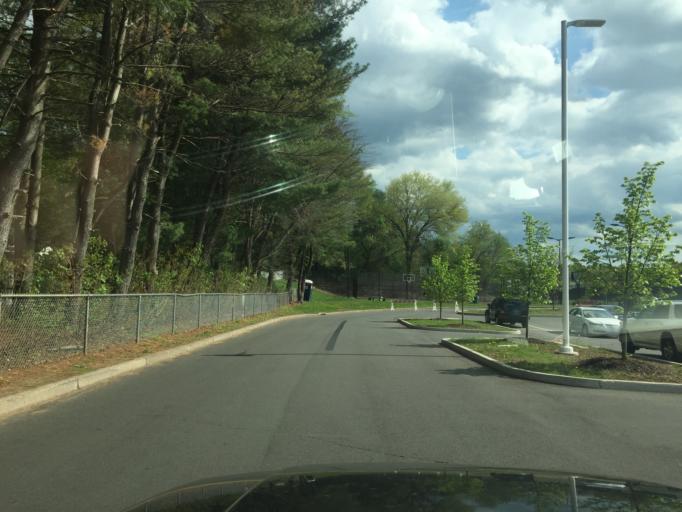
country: US
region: Connecticut
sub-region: Hartford County
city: Kensington
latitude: 41.6217
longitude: -72.7507
